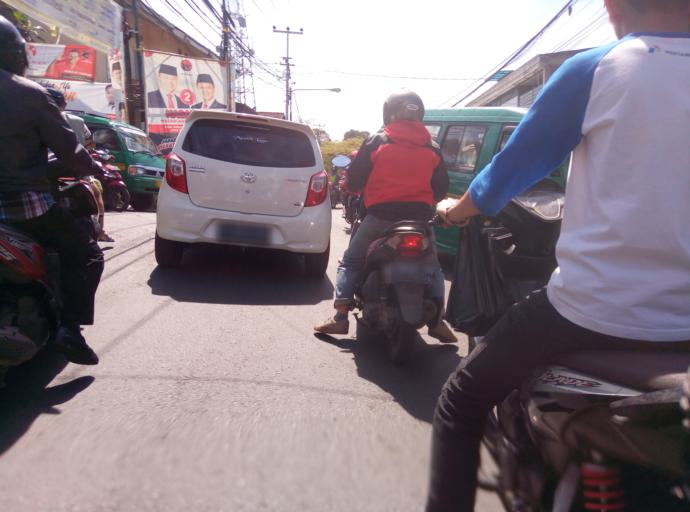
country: ID
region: West Java
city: Bandung
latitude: -6.8913
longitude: 107.6271
